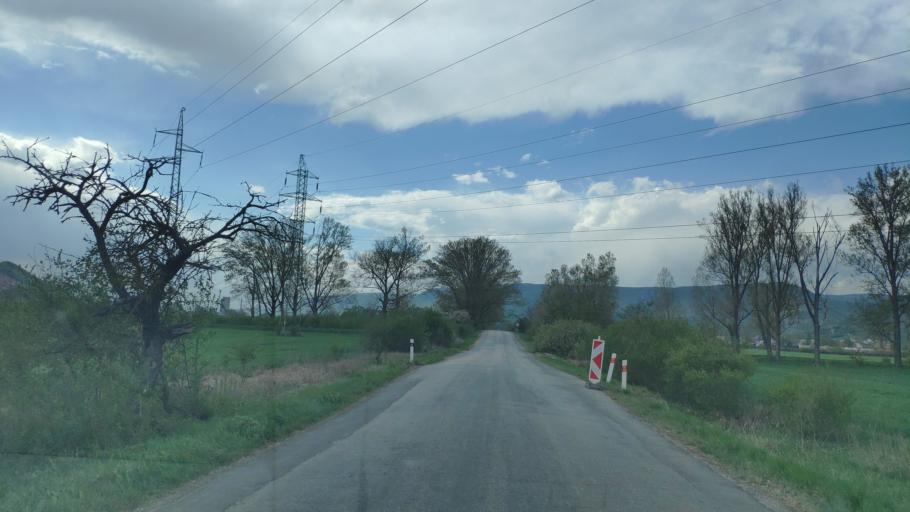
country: SK
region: Kosicky
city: Moldava nad Bodvou
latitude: 48.5931
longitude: 20.8961
